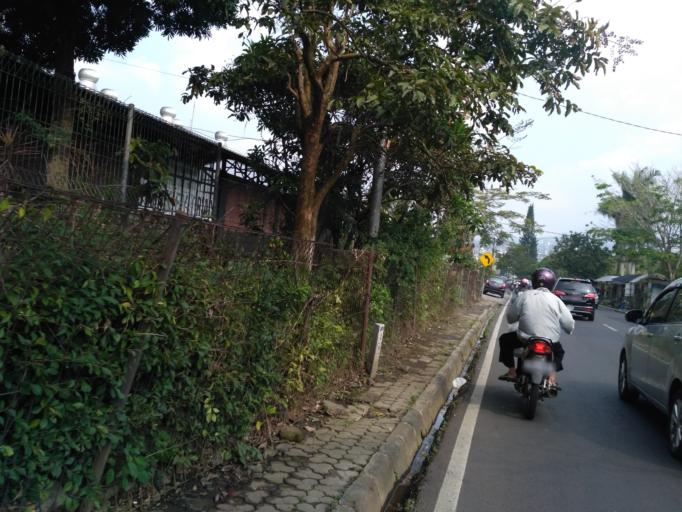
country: ID
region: East Java
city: Batu
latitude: -7.8597
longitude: 112.5269
